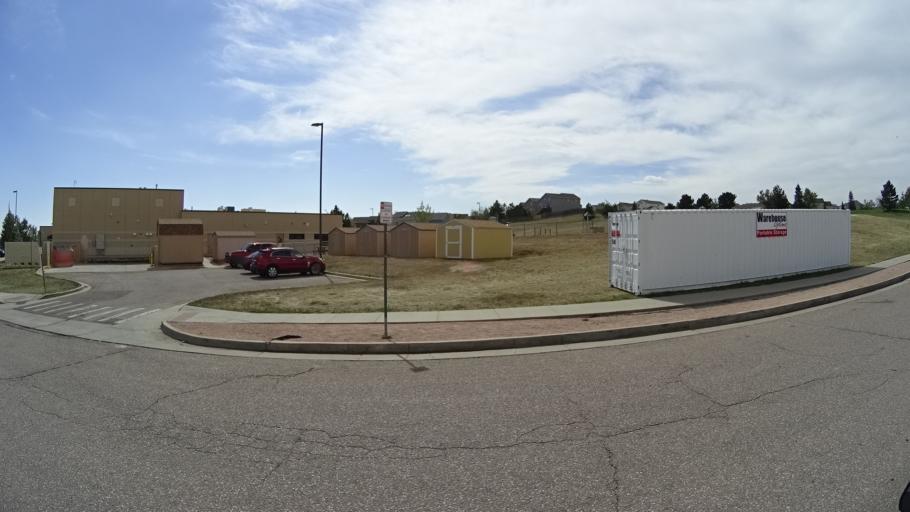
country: US
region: Colorado
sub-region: El Paso County
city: Cimarron Hills
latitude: 38.9069
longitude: -104.7123
